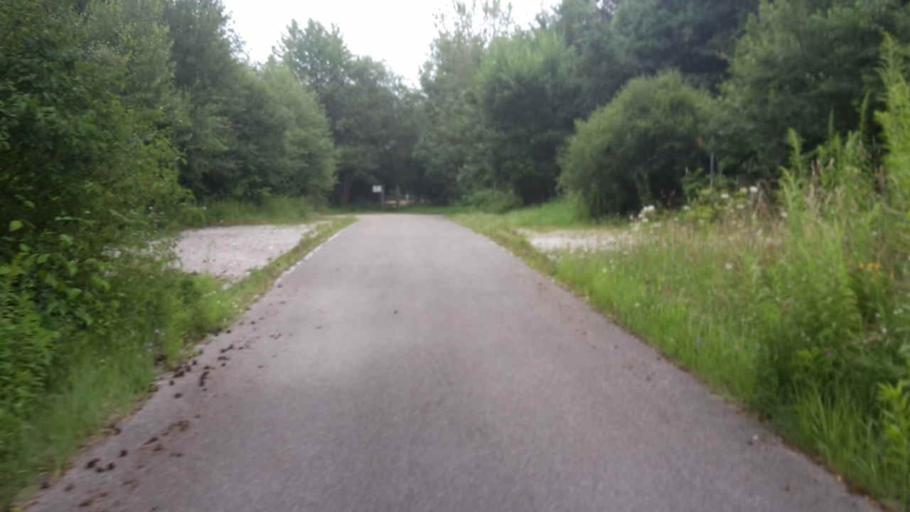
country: DE
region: Bavaria
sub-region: Upper Bavaria
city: Neuried
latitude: 48.0610
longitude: 11.4745
